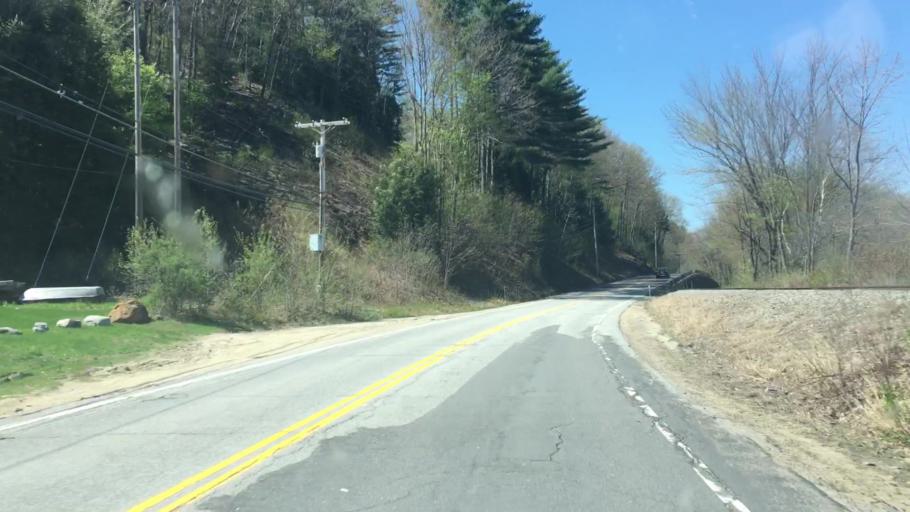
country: US
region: New Hampshire
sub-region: Grafton County
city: Plymouth
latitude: 43.7406
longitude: -71.6781
